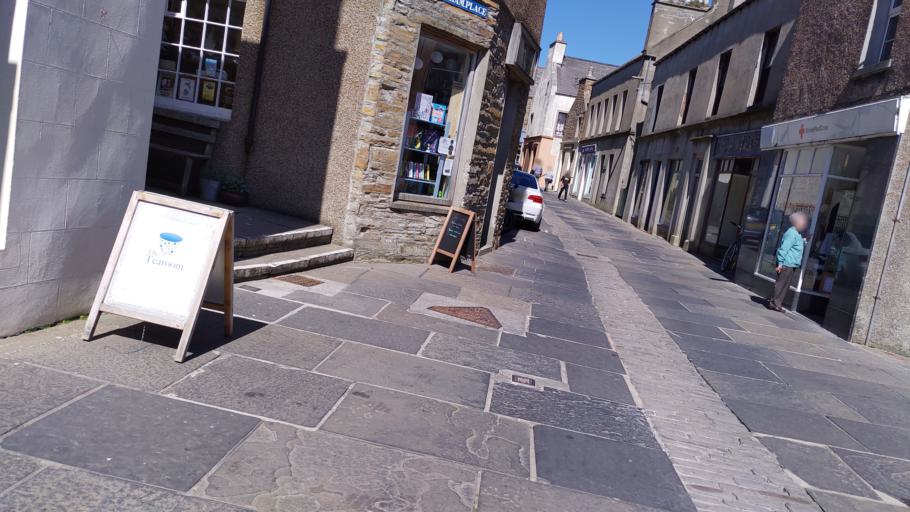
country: GB
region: Scotland
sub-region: Orkney Islands
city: Stromness
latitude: 58.9612
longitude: -3.2998
